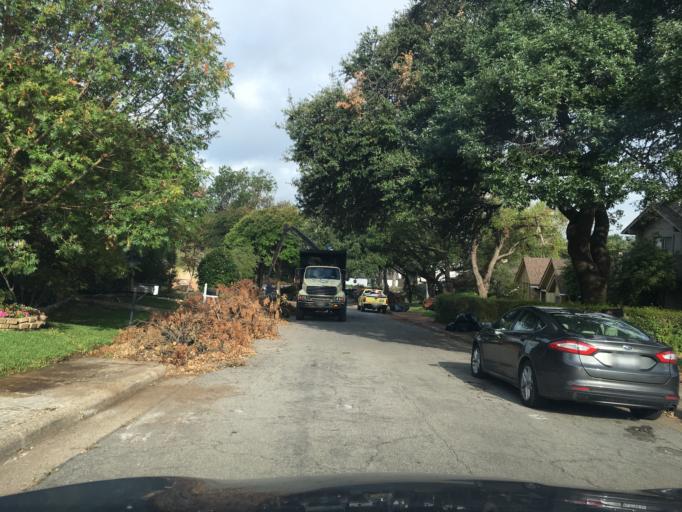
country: US
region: Texas
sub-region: Dallas County
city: Richardson
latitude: 32.8962
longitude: -96.7465
